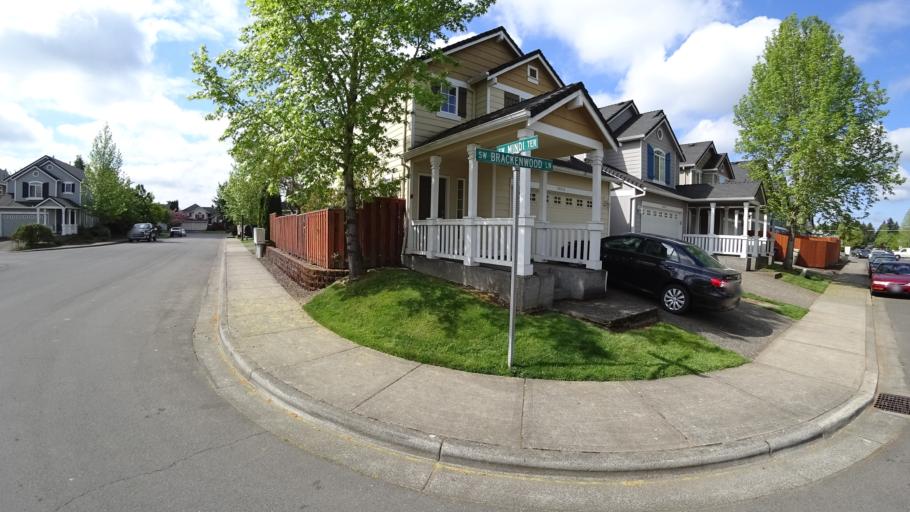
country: US
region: Oregon
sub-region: Washington County
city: Aloha
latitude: 45.5130
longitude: -122.8875
